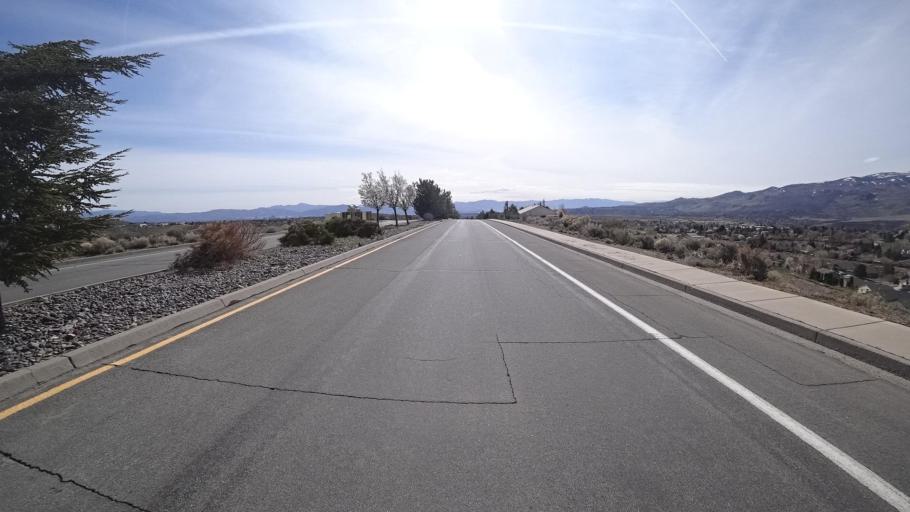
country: US
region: Nevada
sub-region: Washoe County
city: Mogul
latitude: 39.5313
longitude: -119.8981
